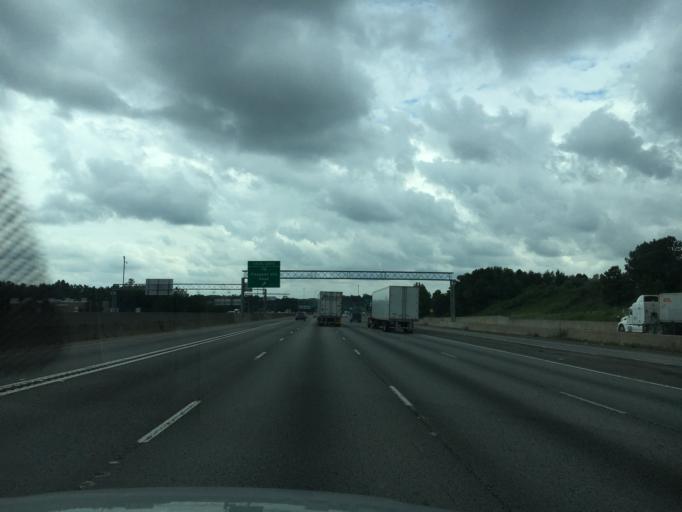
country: US
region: Georgia
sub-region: Gwinnett County
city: Duluth
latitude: 33.9763
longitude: -84.0899
